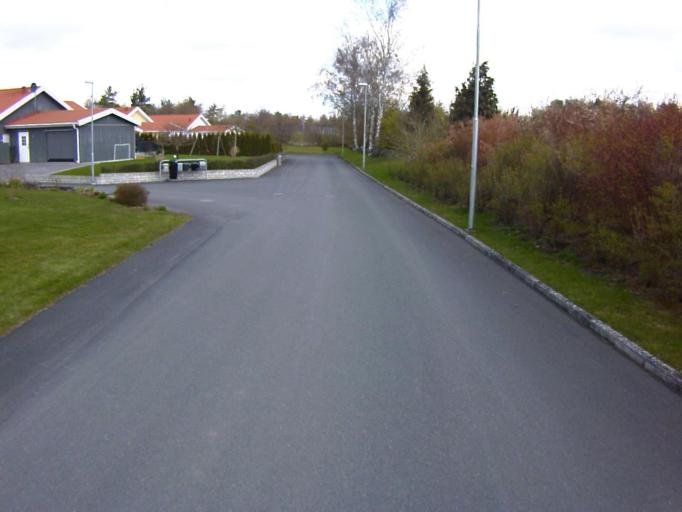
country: SE
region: Skane
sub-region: Kristianstads Kommun
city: Norra Asum
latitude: 56.0053
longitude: 14.0997
